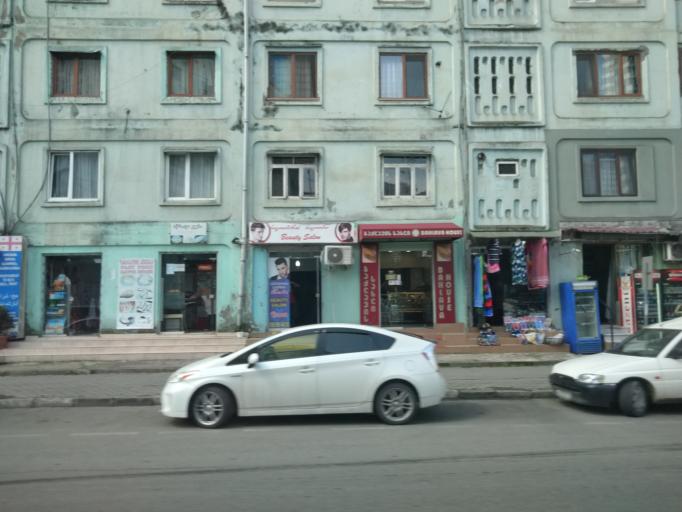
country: GE
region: Ajaria
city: Batumi
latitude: 41.6339
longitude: 41.6098
